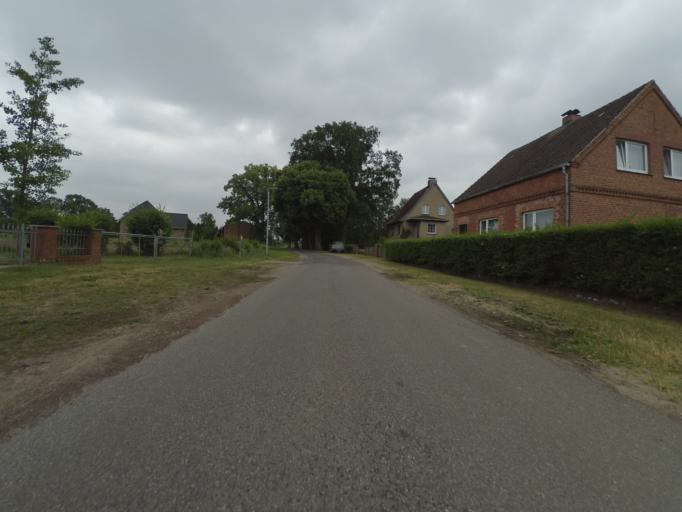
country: DE
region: Mecklenburg-Vorpommern
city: Neustadt-Glewe
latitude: 53.4080
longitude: 11.5763
